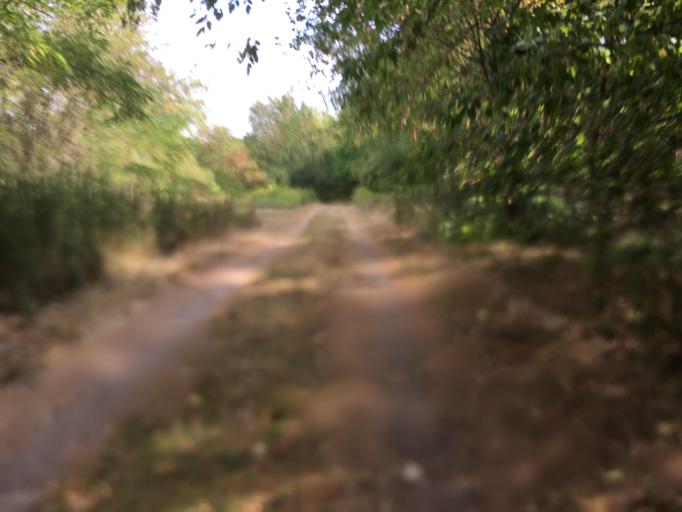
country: DE
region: Brandenburg
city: Zehdenick
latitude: 53.0576
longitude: 13.2876
